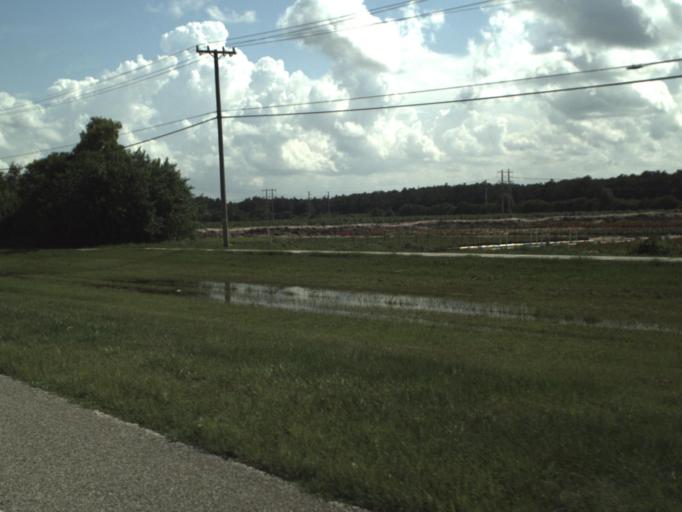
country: US
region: Florida
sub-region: Palm Beach County
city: Villages of Oriole
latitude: 26.5140
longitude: -80.2054
